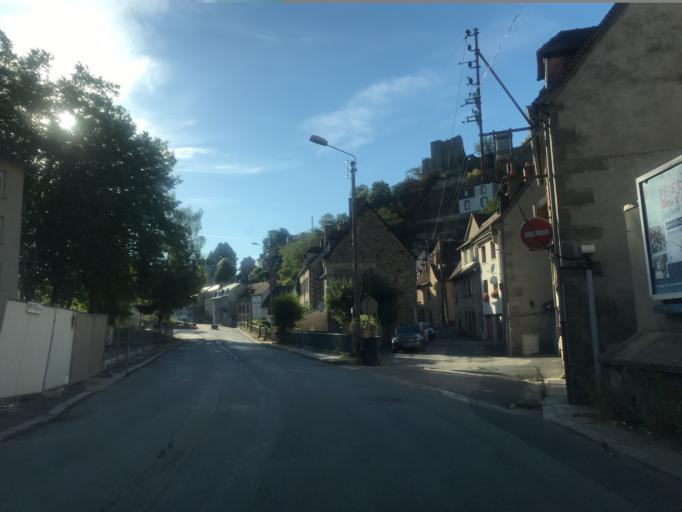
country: FR
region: Limousin
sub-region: Departement de la Creuse
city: Aubusson
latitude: 45.9553
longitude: 2.1738
